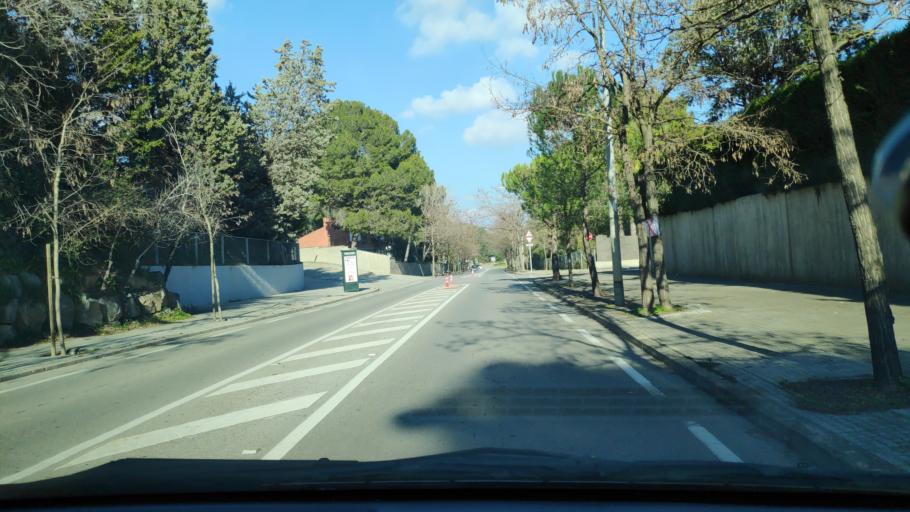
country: ES
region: Catalonia
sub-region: Provincia de Barcelona
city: Sant Quirze del Valles
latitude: 41.5069
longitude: 2.0897
